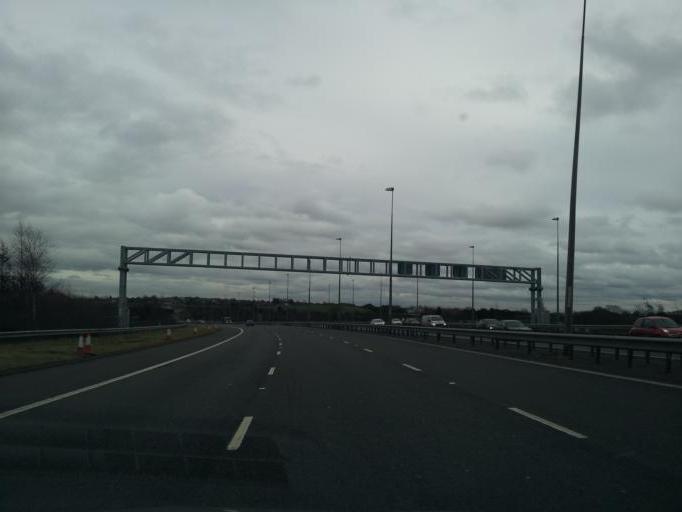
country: GB
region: England
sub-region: Staffordshire
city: Featherstone
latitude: 52.6658
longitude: -2.0667
